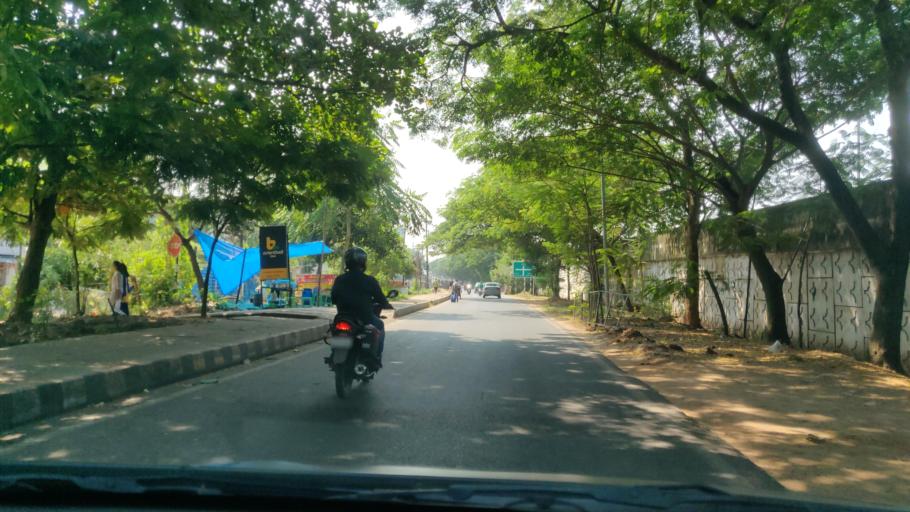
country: IN
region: Odisha
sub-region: Khordha
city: Bhubaneshwar
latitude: 20.2962
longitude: 85.8269
